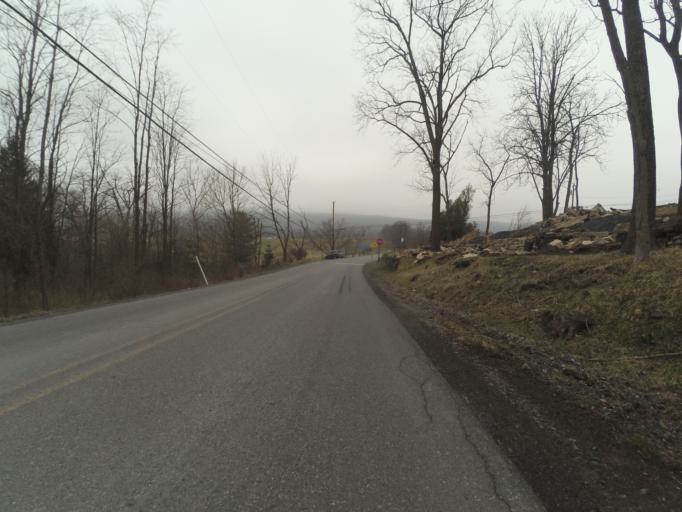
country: US
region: Pennsylvania
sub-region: Centre County
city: Boalsburg
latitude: 40.7993
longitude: -77.7625
